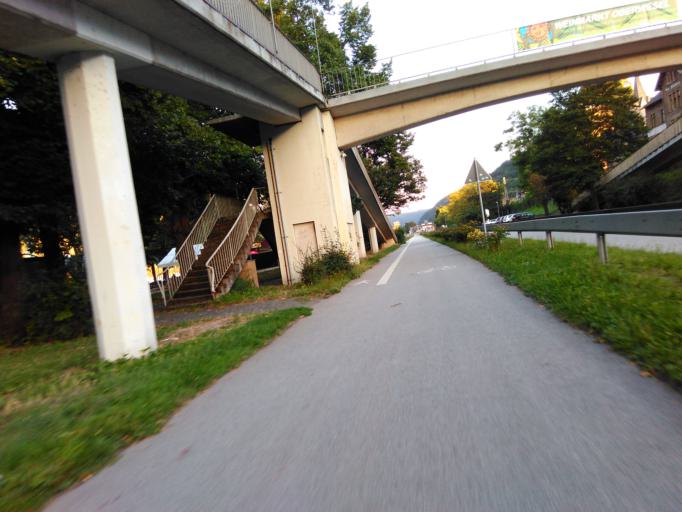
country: DE
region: Rheinland-Pfalz
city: Oberwesel
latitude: 50.1077
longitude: 7.7281
